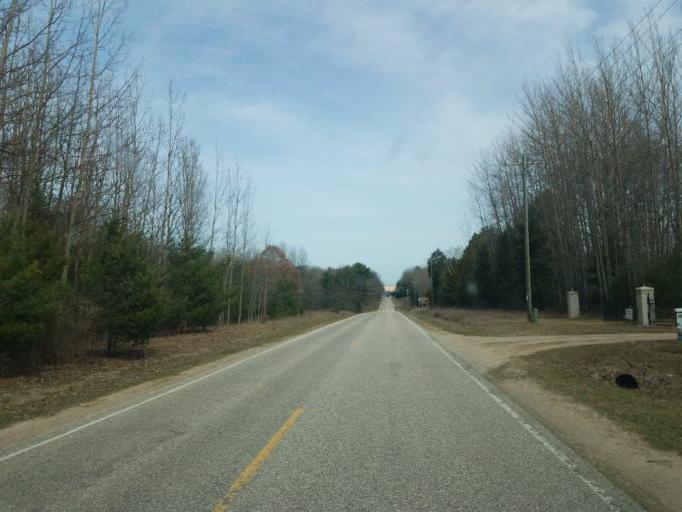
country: US
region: Michigan
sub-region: Oceana County
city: Shelby
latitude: 43.6497
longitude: -86.5128
